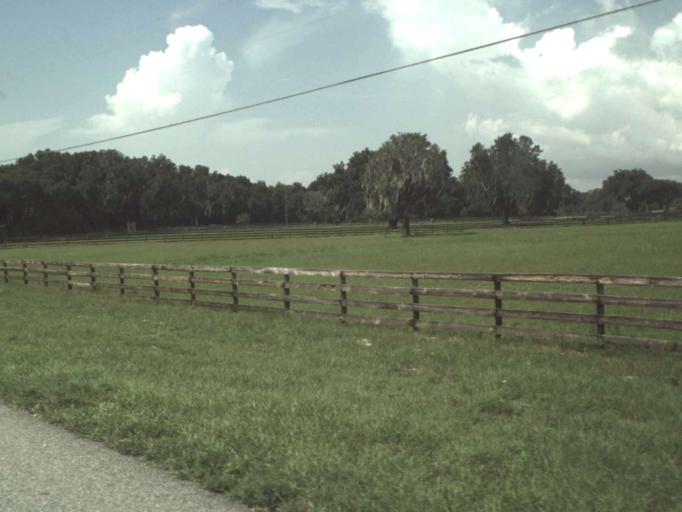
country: US
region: Florida
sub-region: Sumter County
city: Lake Panasoffkee
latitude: 28.7820
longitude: -82.0681
